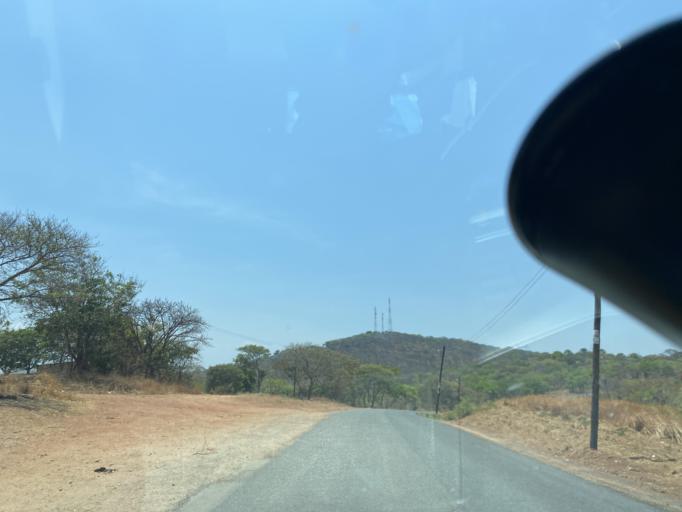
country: ZM
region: Lusaka
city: Kafue
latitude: -15.8660
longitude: 28.4411
